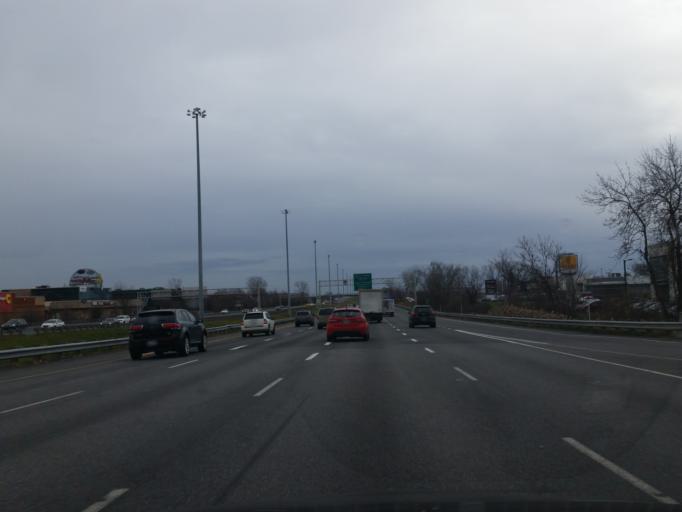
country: CA
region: Quebec
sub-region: Laurentides
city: Blainville
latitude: 45.6440
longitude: -73.8651
